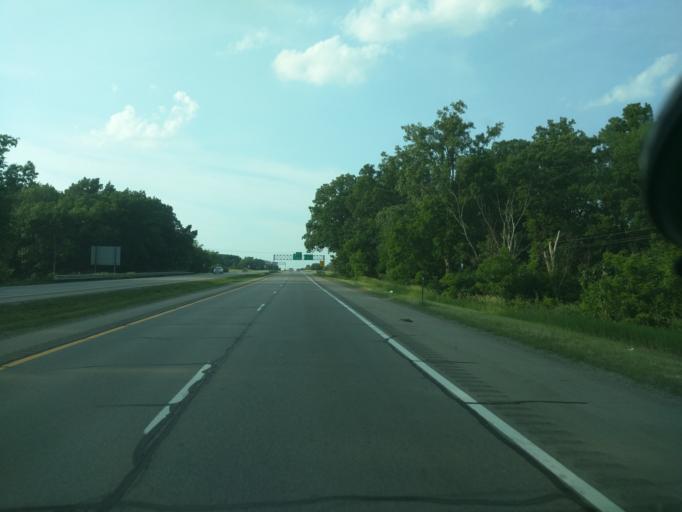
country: US
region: Michigan
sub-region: Jackson County
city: Jackson
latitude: 42.2858
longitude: -84.4326
